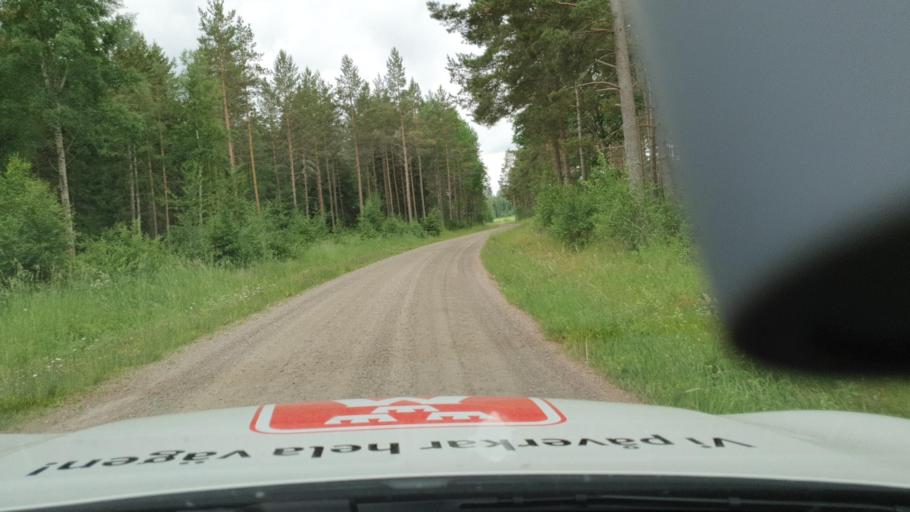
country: SE
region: Vaestra Goetaland
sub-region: Tidaholms Kommun
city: Olofstorp
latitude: 58.1645
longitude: 14.0737
